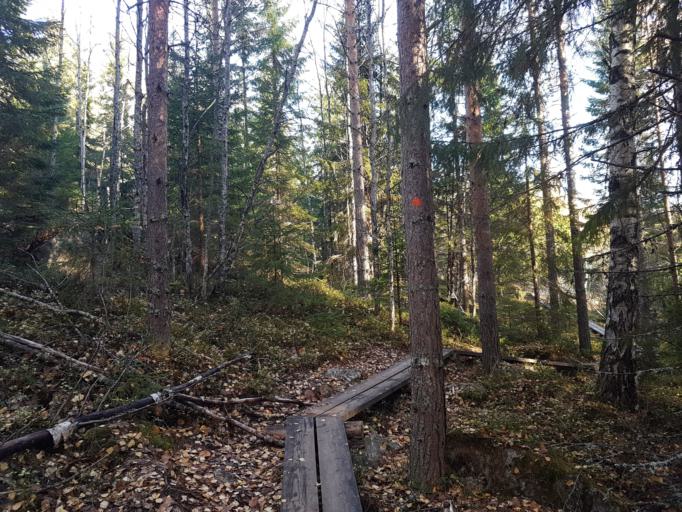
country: SE
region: Vaesternorrland
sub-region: OErnskoeldsviks Kommun
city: Kopmanholmen
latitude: 63.0887
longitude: 18.4948
